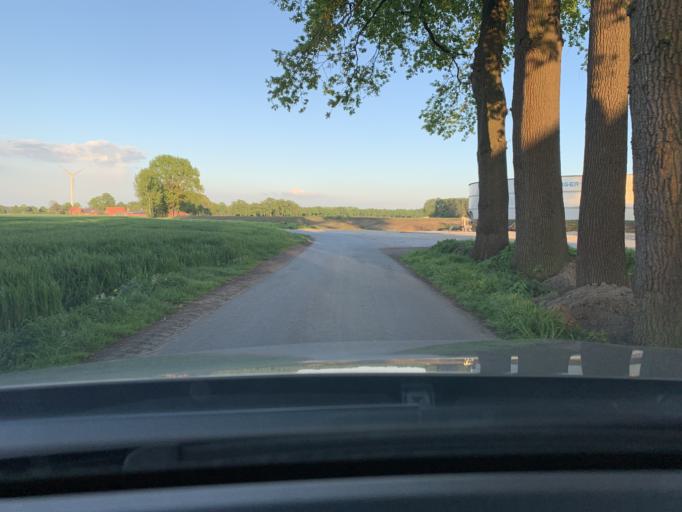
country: DE
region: North Rhine-Westphalia
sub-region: Regierungsbezirk Detmold
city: Langenberg
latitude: 51.8219
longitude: 8.3659
